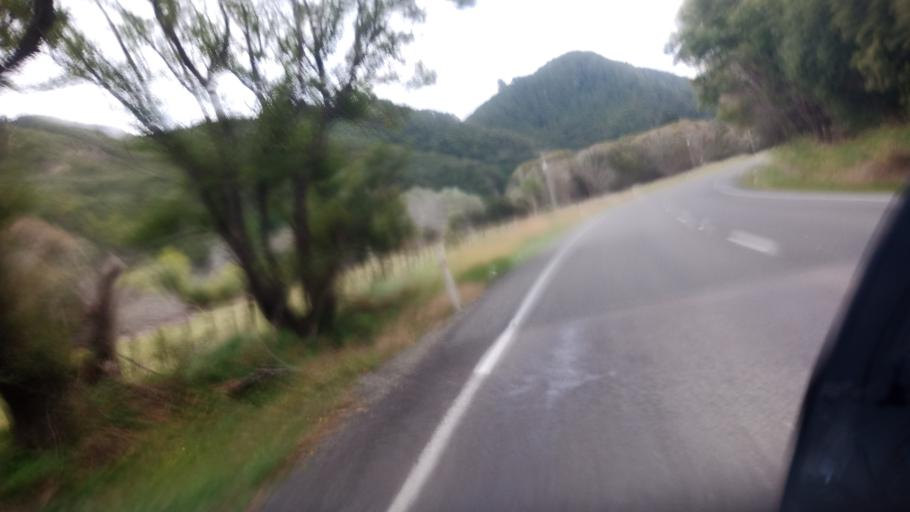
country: NZ
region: Gisborne
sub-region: Gisborne District
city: Gisborne
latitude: -38.2907
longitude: 178.2664
